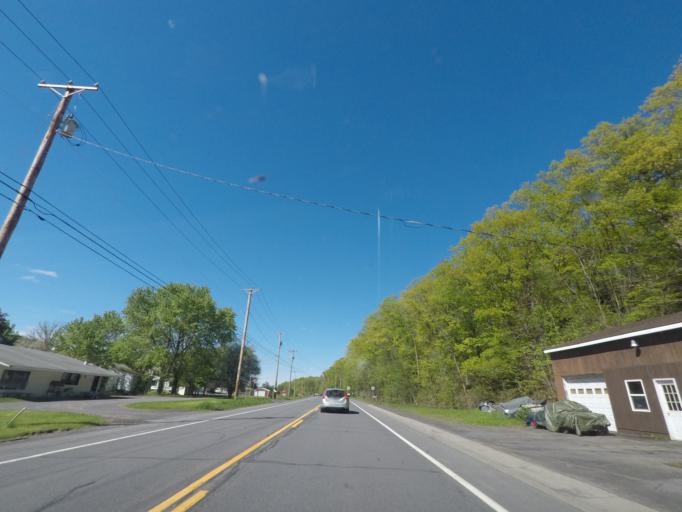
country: US
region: New York
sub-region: Albany County
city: Ravena
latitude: 42.4277
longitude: -73.8165
